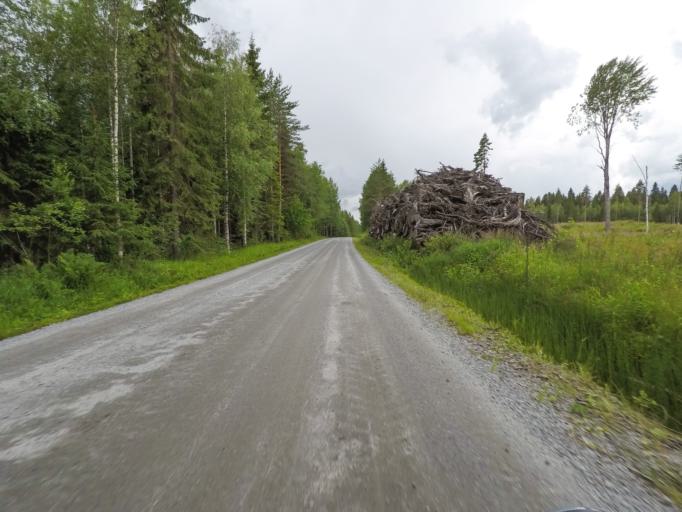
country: FI
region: Central Finland
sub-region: Jyvaeskylae
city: Hankasalmi
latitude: 62.4180
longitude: 26.6391
